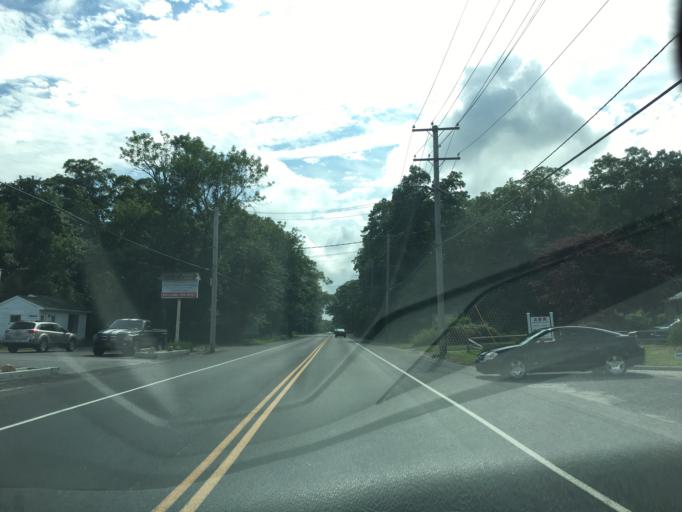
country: US
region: New York
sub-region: Suffolk County
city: Greenport West
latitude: 41.0989
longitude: -72.3752
